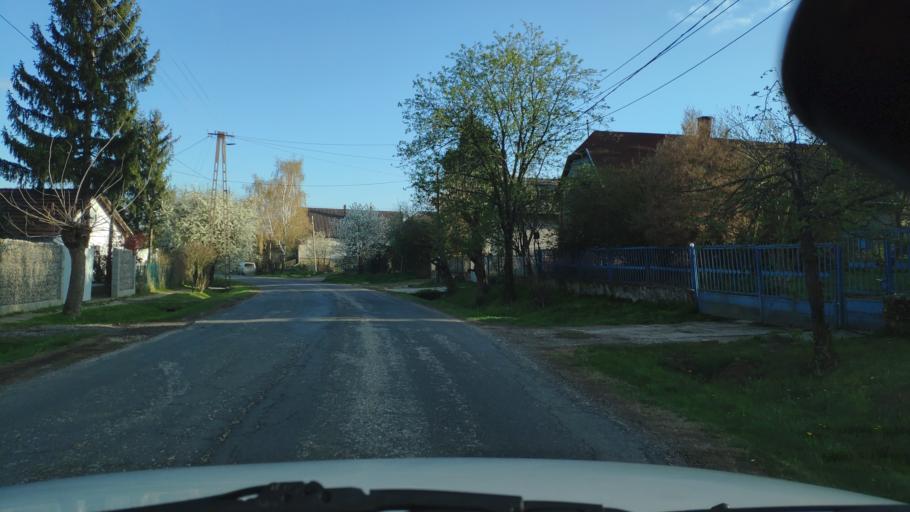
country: HU
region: Zala
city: Zalakomar
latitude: 46.4424
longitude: 17.1207
